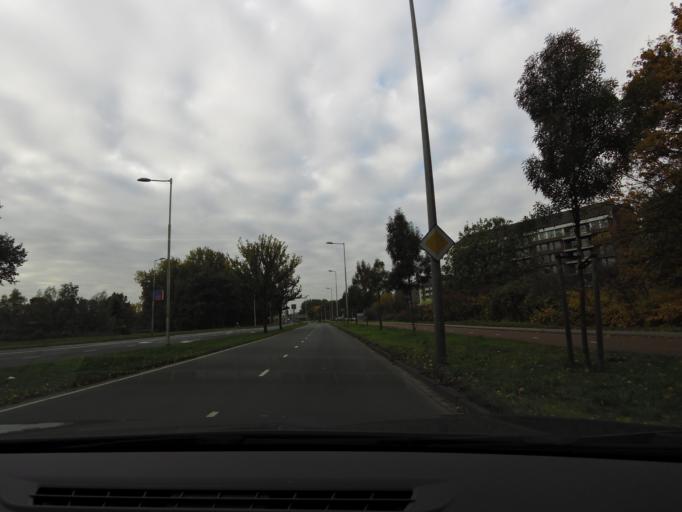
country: NL
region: South Holland
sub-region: Gemeente Rotterdam
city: Delfshaven
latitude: 51.8752
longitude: 4.4596
